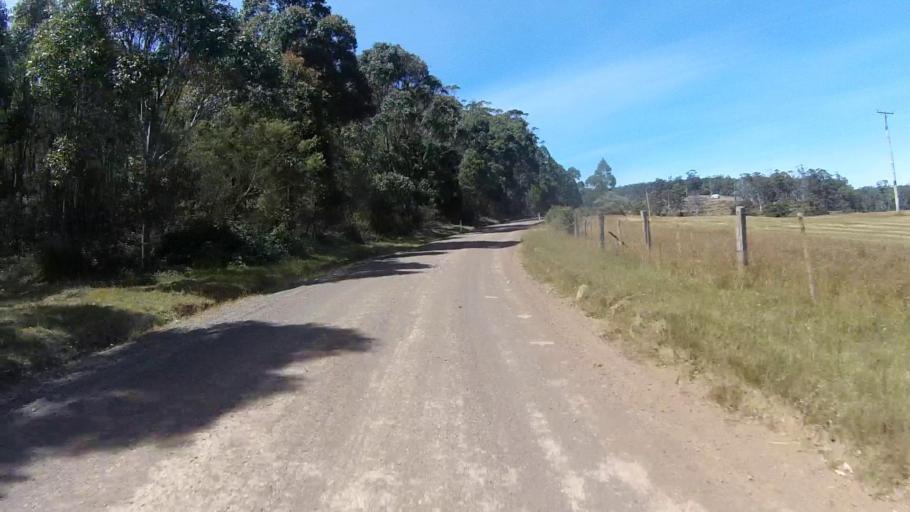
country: AU
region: Tasmania
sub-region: Sorell
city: Sorell
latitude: -42.6968
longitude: 147.7404
